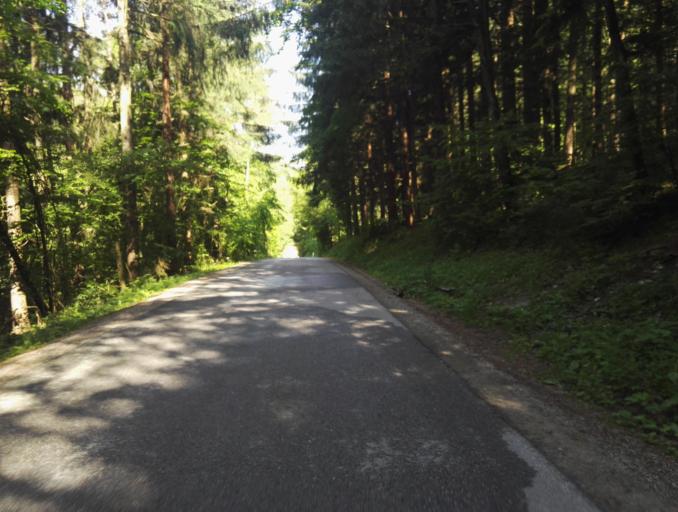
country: AT
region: Styria
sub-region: Politischer Bezirk Graz-Umgebung
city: Stattegg
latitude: 47.1667
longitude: 15.4212
